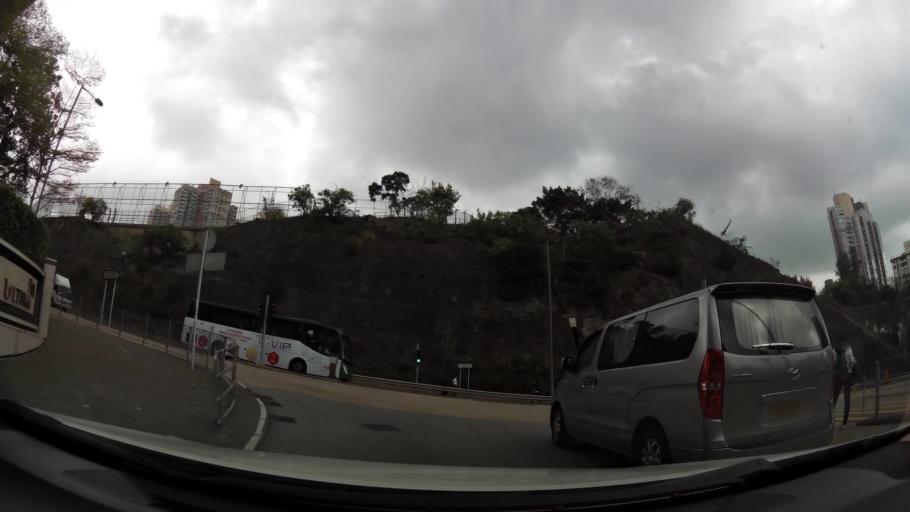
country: HK
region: Kowloon City
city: Kowloon
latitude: 22.3116
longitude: 114.1826
